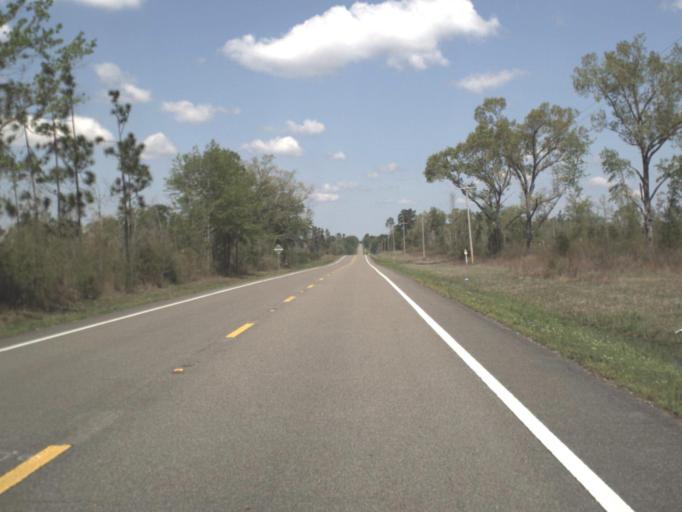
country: US
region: Alabama
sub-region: Escambia County
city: East Brewton
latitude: 30.9121
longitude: -87.0400
